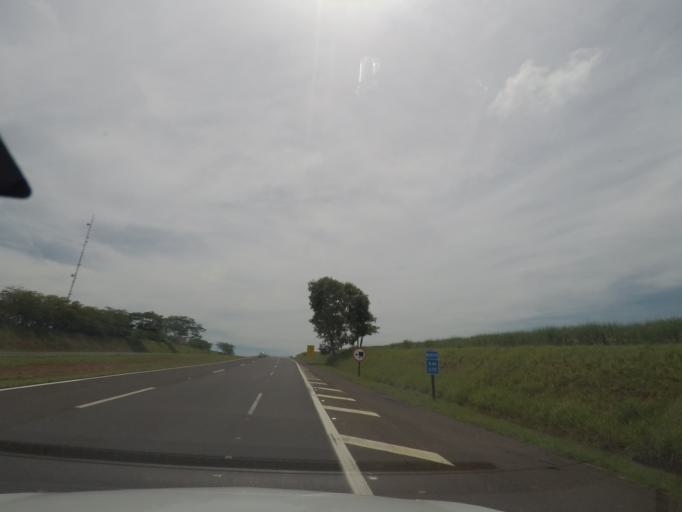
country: BR
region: Sao Paulo
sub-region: Bebedouro
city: Bebedouro
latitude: -20.9692
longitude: -48.4406
